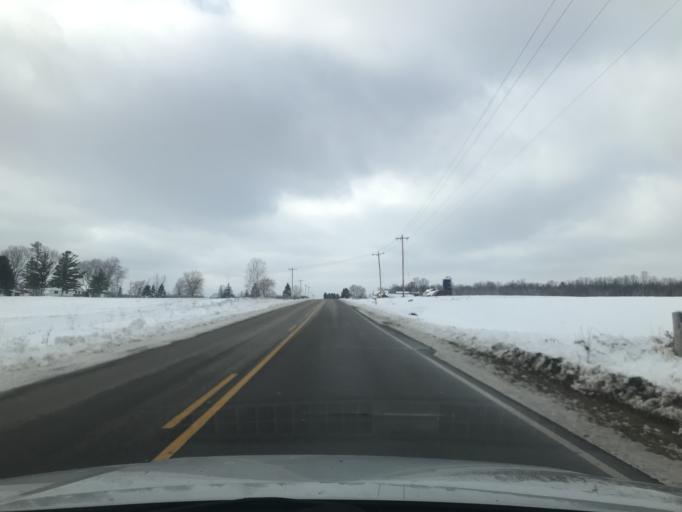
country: US
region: Wisconsin
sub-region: Oconto County
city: Oconto
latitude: 44.9501
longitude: -87.9594
